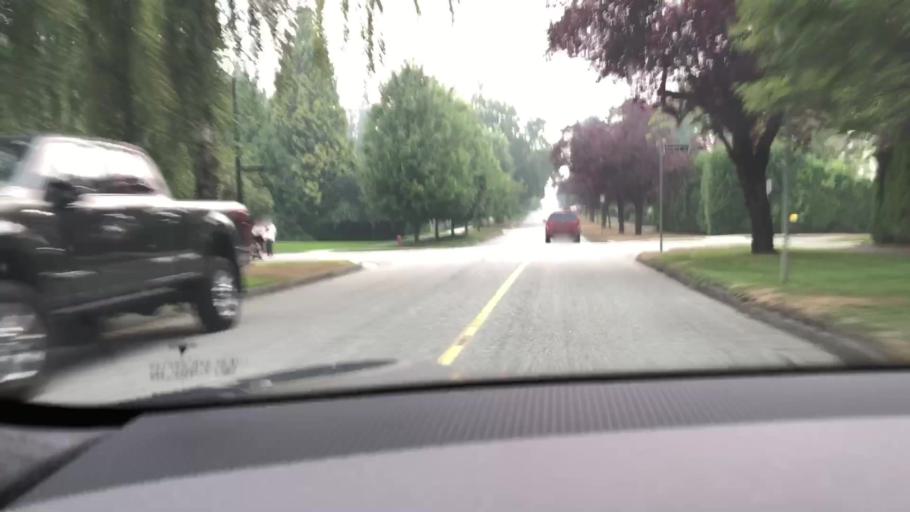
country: CA
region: British Columbia
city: Vancouver
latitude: 49.2416
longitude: -123.1318
